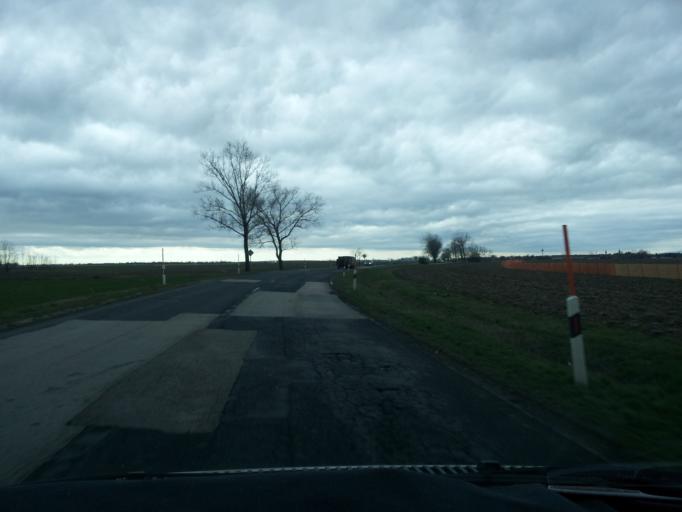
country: HU
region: Gyor-Moson-Sopron
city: Beled
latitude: 47.4739
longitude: 17.1327
